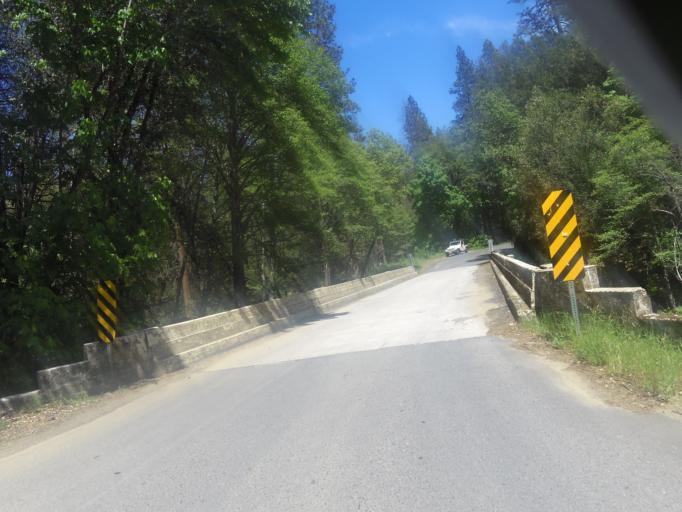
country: US
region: California
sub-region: Mariposa County
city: Midpines
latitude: 37.5169
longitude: -119.8379
